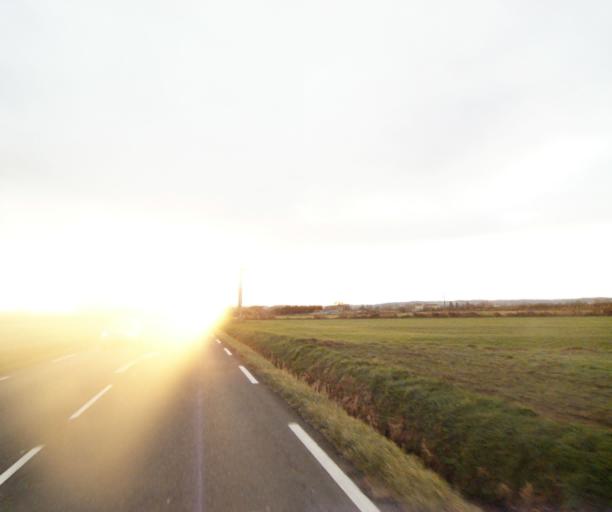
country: FR
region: Rhone-Alpes
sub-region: Departement de la Loire
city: Sury-le-Comtal
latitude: 45.5481
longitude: 4.1688
